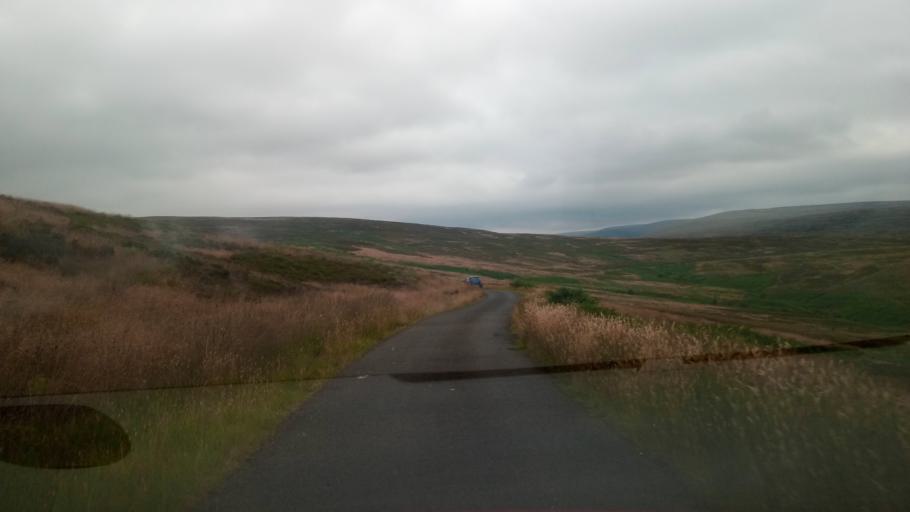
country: GB
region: Scotland
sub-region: Dumfries and Galloway
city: Langholm
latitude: 55.1646
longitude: -2.9621
